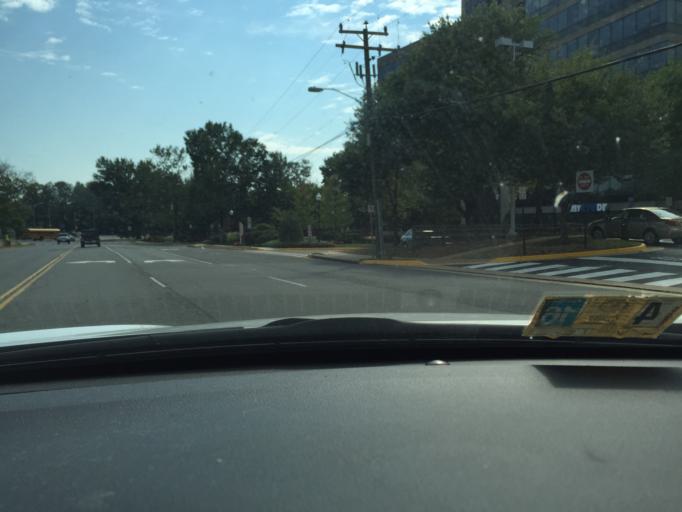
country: US
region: Virginia
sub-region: Fairfax County
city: Tysons Corner
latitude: 38.9115
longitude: -77.2221
